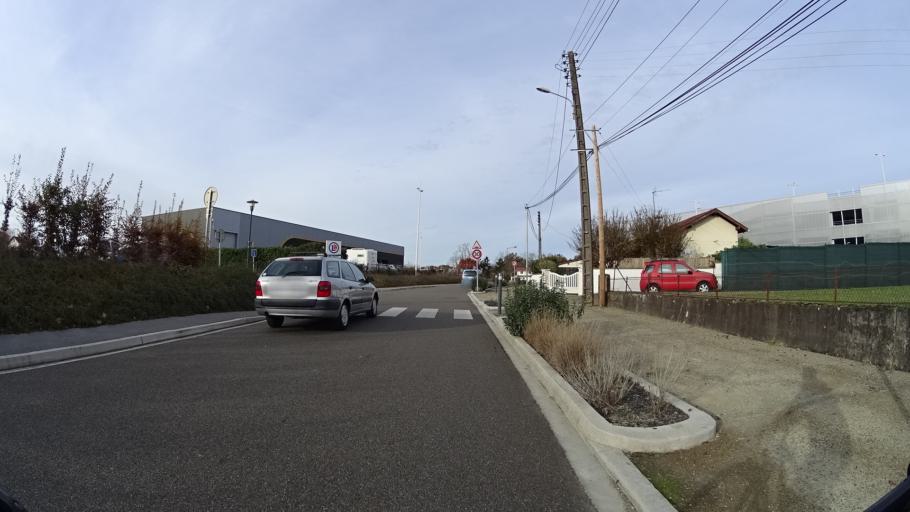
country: FR
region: Aquitaine
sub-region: Departement des Landes
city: Saint-Paul-les-Dax
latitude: 43.7310
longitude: -1.0449
